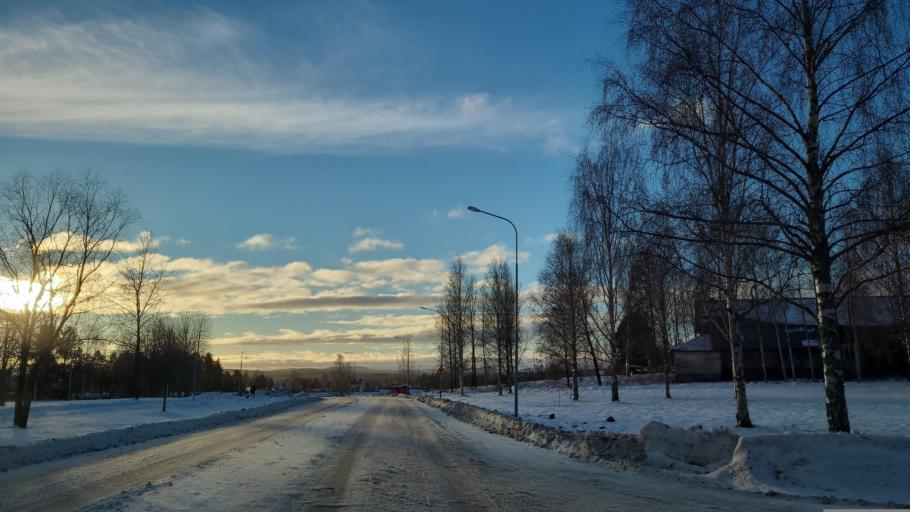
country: SE
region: Gaevleborg
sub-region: Bollnas Kommun
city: Bollnas
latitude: 61.3604
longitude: 16.4211
